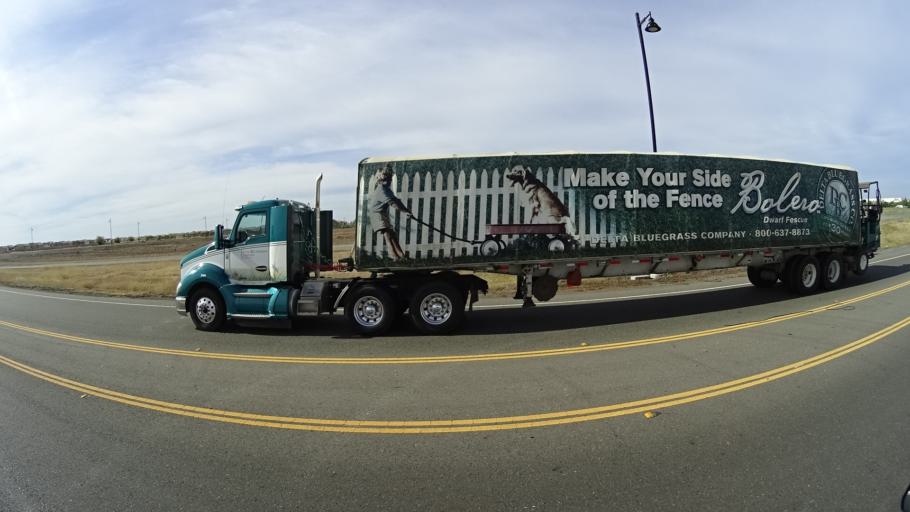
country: US
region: California
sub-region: Placer County
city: Lincoln
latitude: 38.8316
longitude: -121.2952
